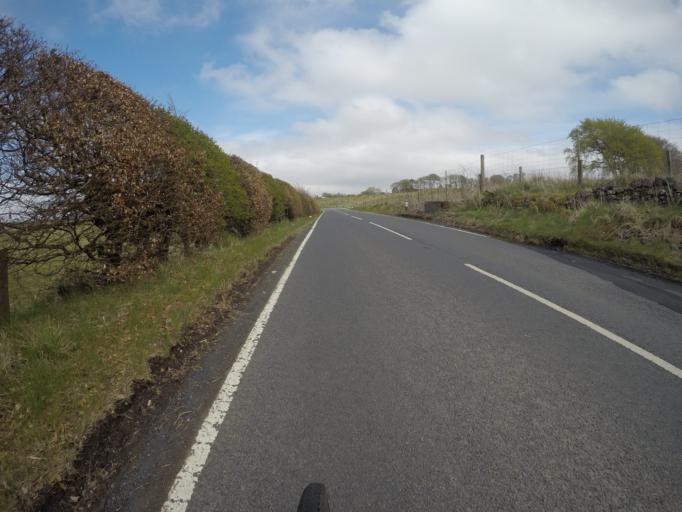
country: GB
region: Scotland
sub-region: East Renfrewshire
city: Neilston
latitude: 55.7203
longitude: -4.4317
